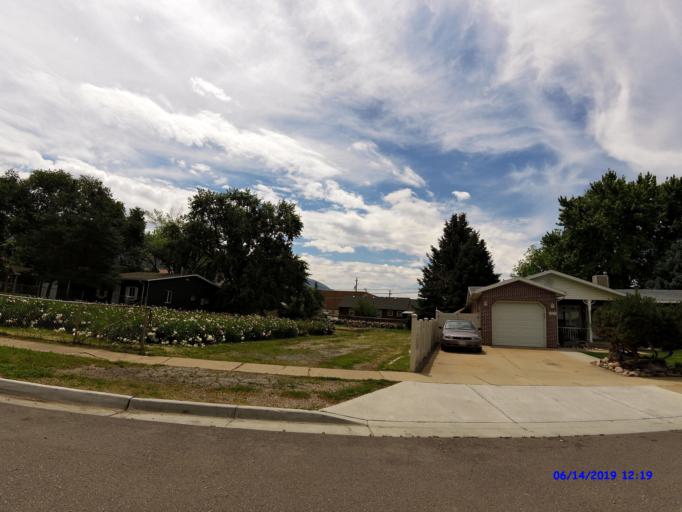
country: US
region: Utah
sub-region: Weber County
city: Ogden
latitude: 41.2524
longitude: -111.9514
